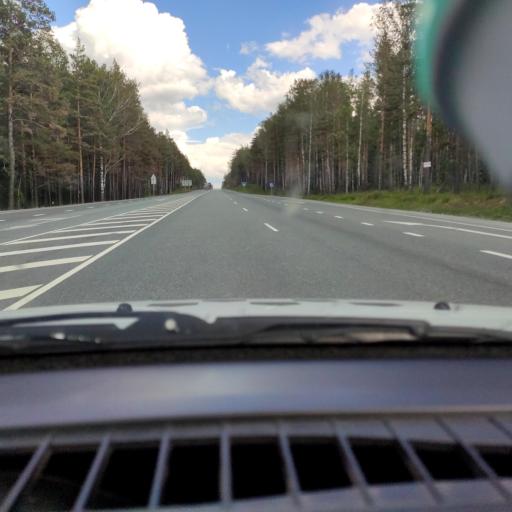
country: RU
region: Chelyabinsk
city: Zlatoust
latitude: 55.0566
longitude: 59.6640
